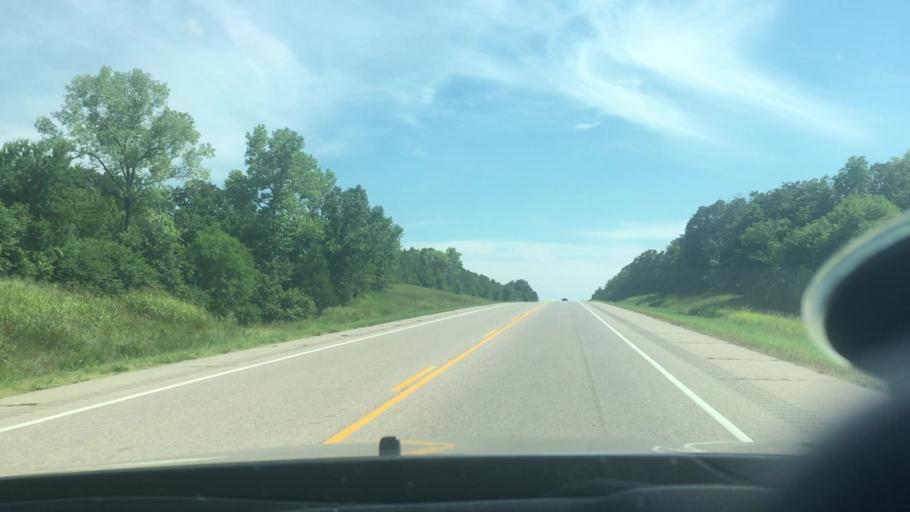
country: US
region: Oklahoma
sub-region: Seminole County
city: Maud
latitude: 35.1066
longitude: -96.6789
